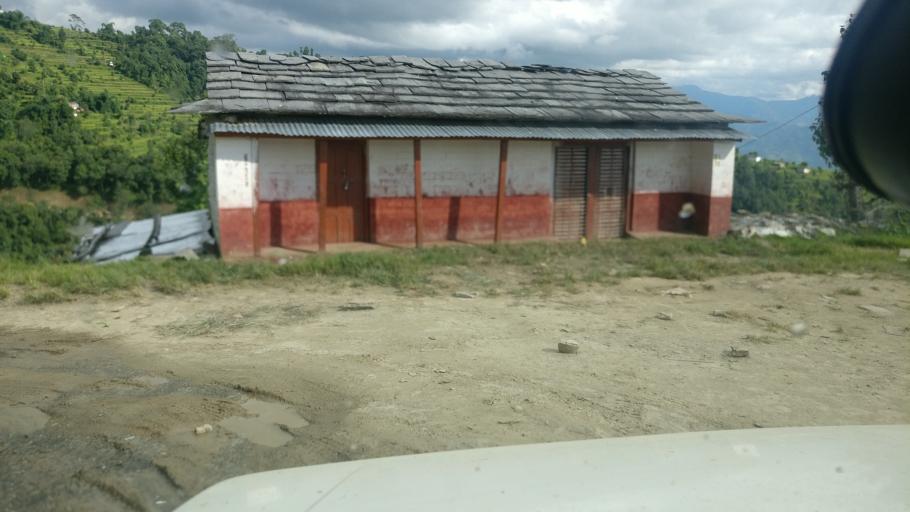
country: NP
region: Western Region
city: Baglung
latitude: 28.2718
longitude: 83.6452
